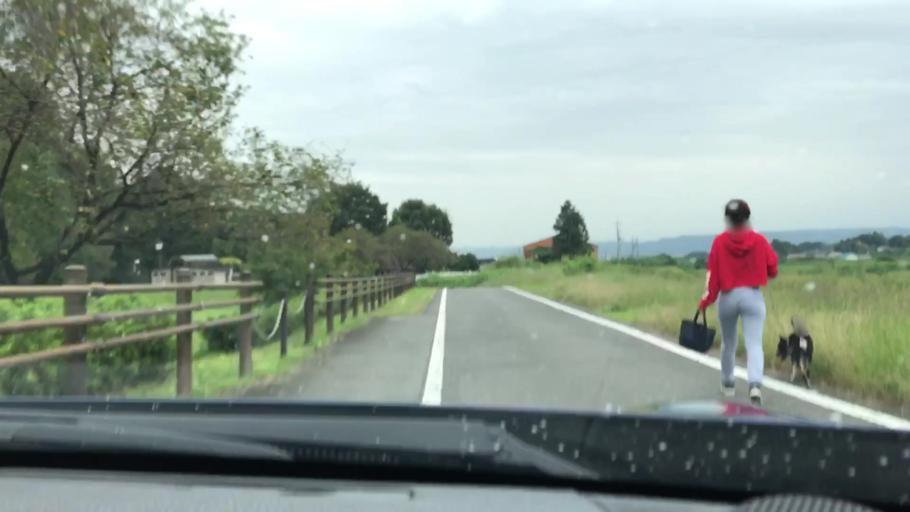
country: JP
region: Gunma
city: Kanekomachi
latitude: 36.3958
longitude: 138.9508
